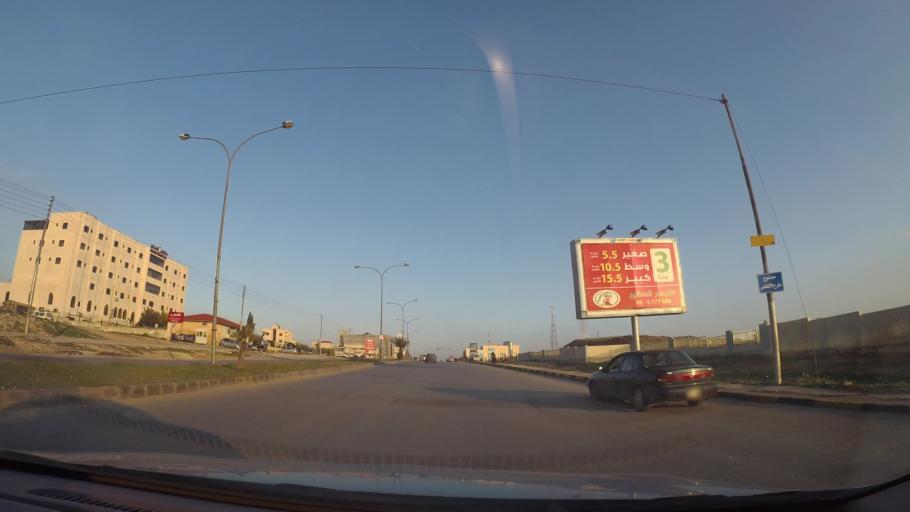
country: JO
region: Amman
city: Al Quwaysimah
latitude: 31.9090
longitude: 35.9278
